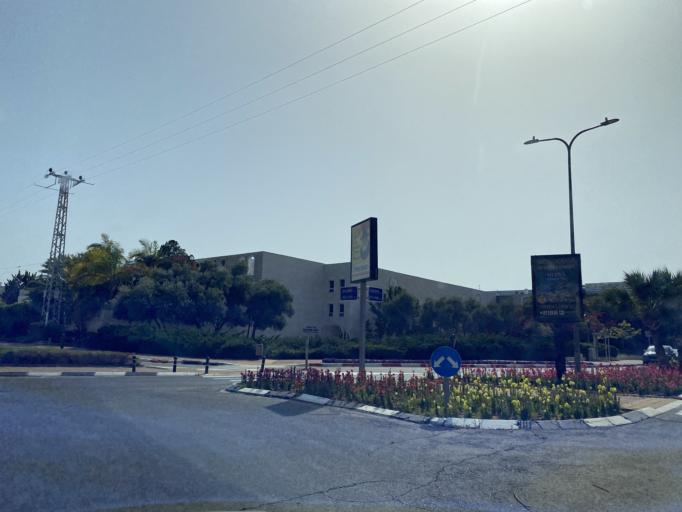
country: IL
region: Tel Aviv
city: Herzliya Pituah
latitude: 32.1680
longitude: 34.8058
